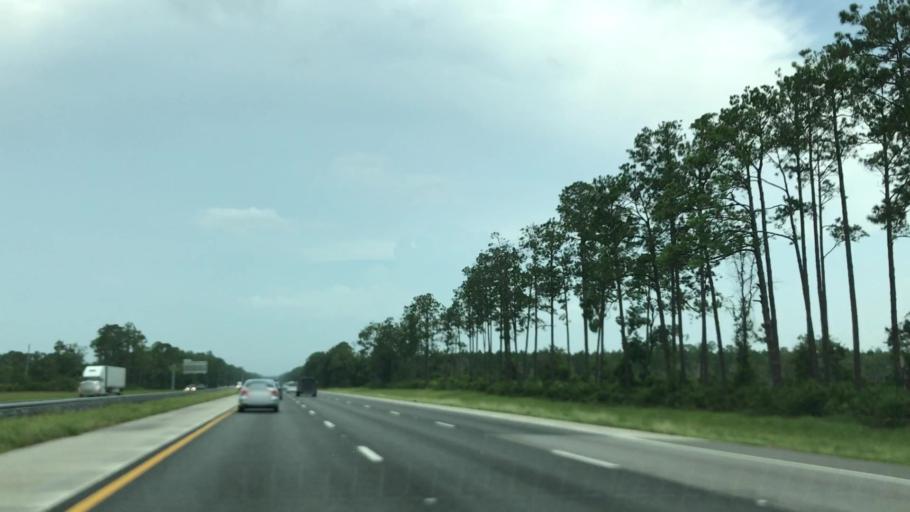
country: US
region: Florida
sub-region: Saint Johns County
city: Saint Augustine
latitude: 29.9314
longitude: -81.4211
